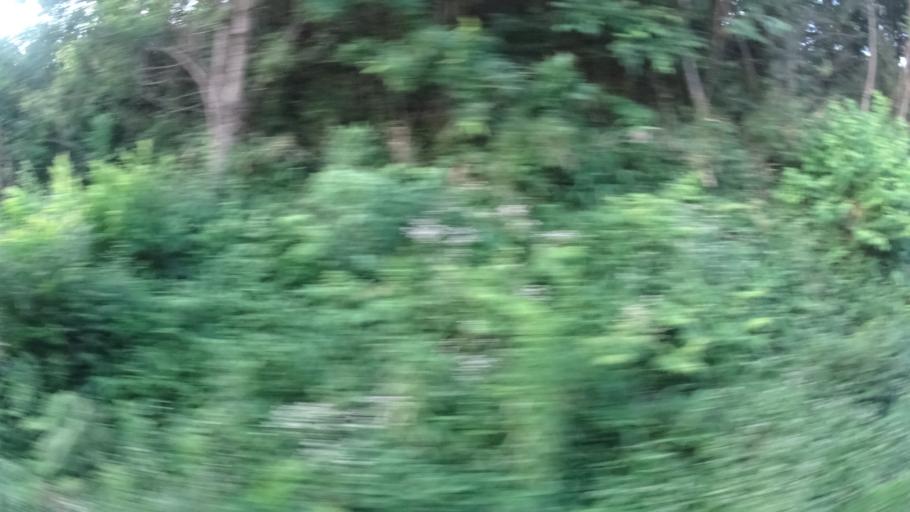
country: JP
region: Fukushima
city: Funehikimachi-funehiki
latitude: 37.4473
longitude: 140.5662
